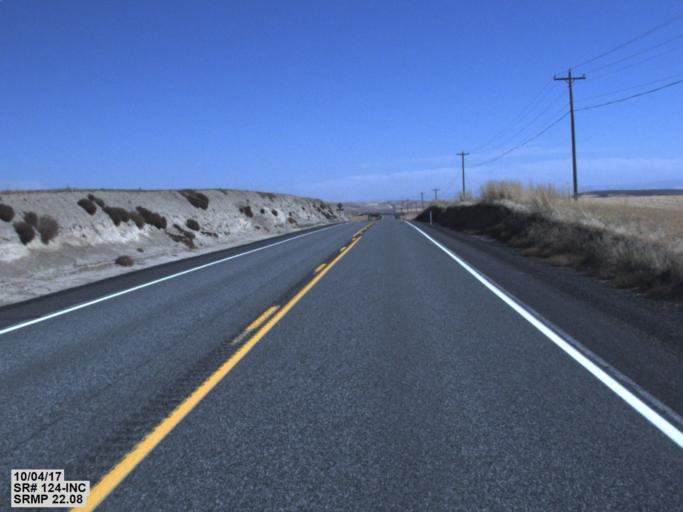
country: US
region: Washington
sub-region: Walla Walla County
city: Garrett
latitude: 46.2962
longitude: -118.5948
